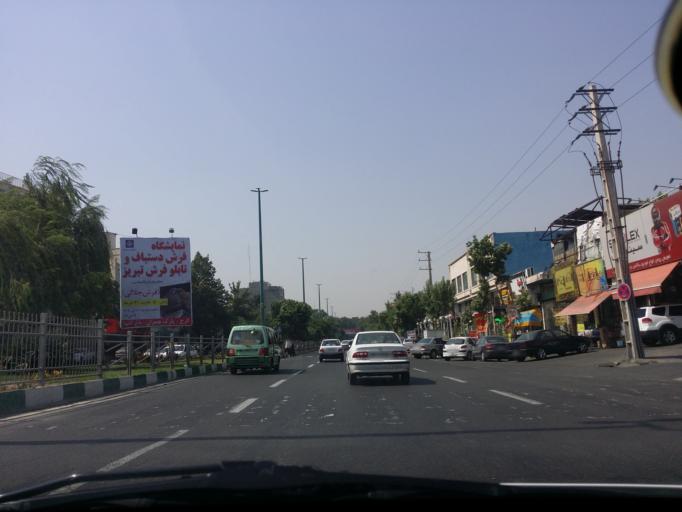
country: IR
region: Alborz
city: Karaj
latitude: 35.7984
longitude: 51.0016
